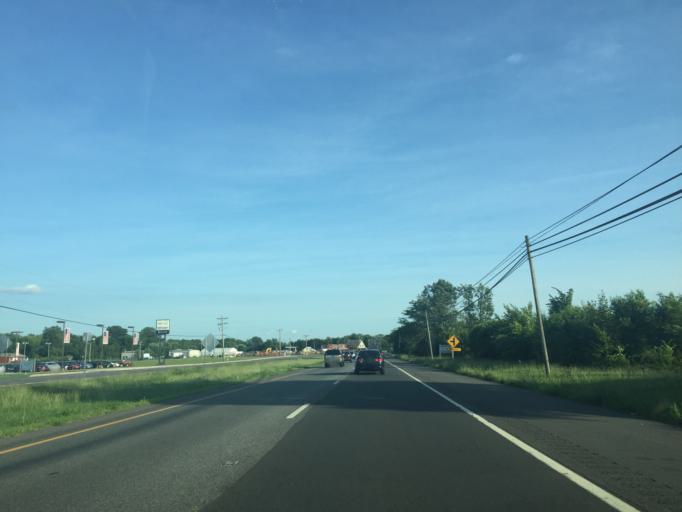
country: US
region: Delaware
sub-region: Kent County
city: Smyrna
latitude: 39.2668
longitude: -75.5877
